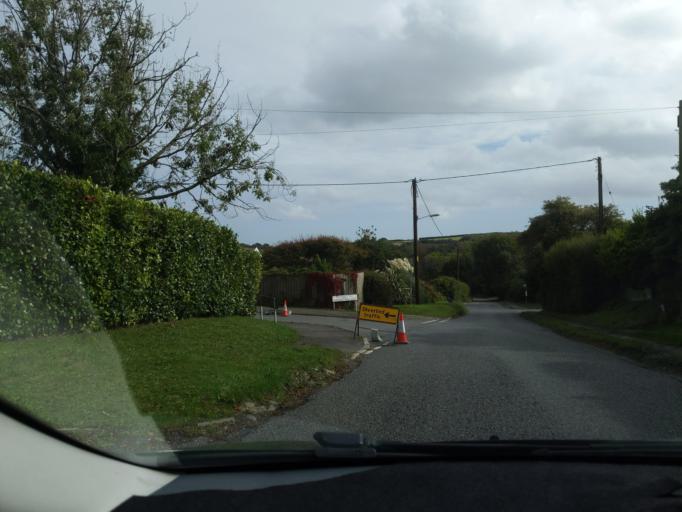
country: GB
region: England
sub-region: Cornwall
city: Mevagissey
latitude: 50.2422
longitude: -4.7989
